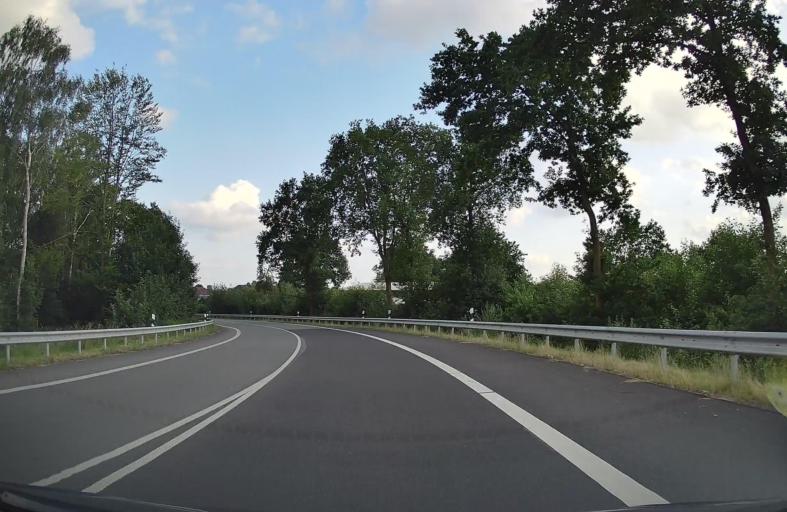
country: DE
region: Lower Saxony
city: Friesoythe
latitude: 53.0181
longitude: 7.8514
